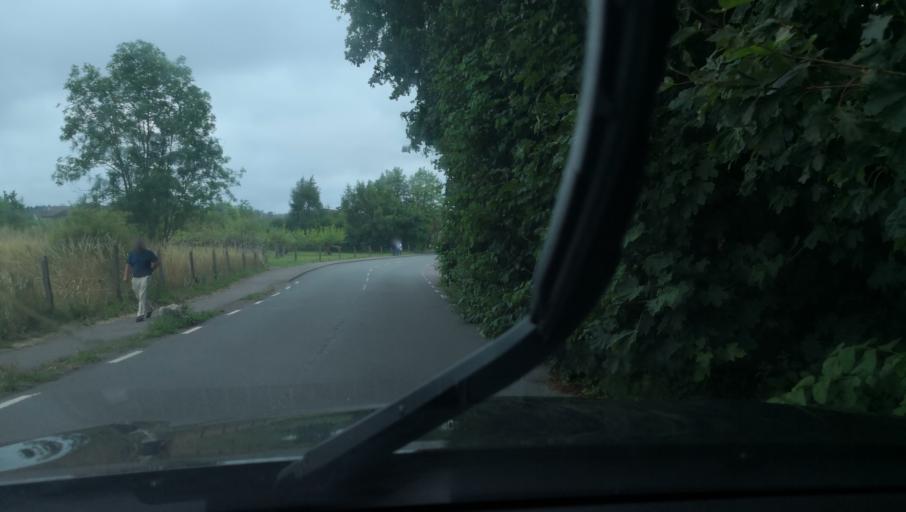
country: SE
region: Skane
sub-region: Simrishamns Kommun
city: Kivik
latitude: 55.6830
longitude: 14.2341
